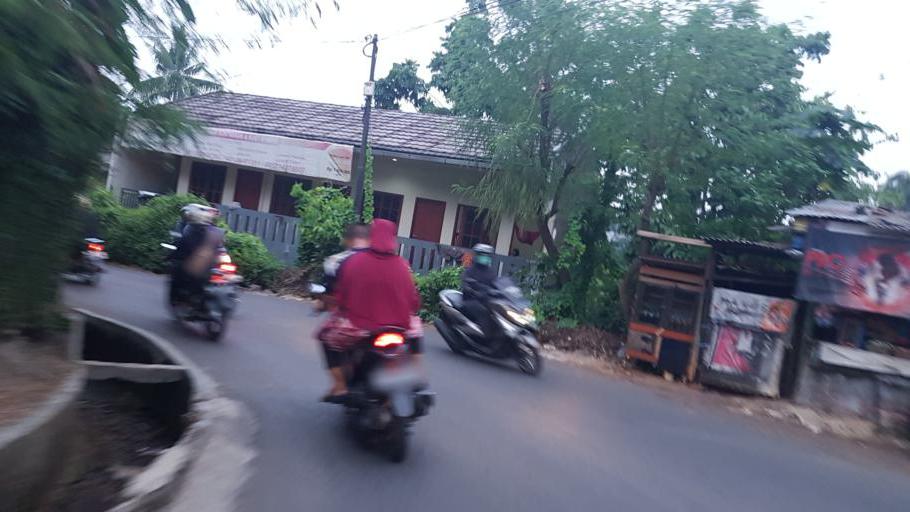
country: ID
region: West Java
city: Depok
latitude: -6.3645
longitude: 106.7999
